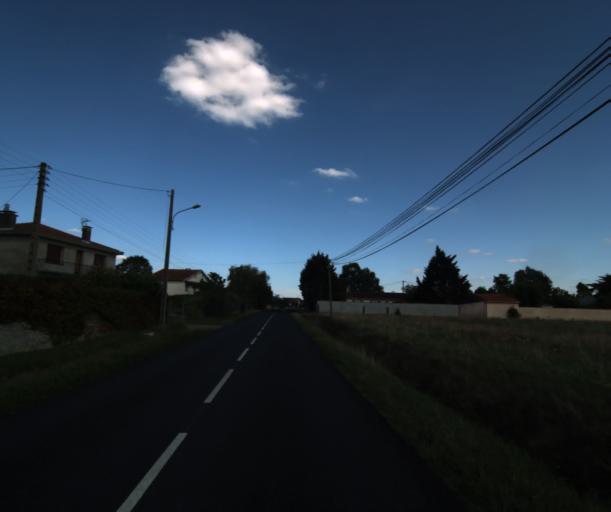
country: FR
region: Midi-Pyrenees
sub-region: Departement de la Haute-Garonne
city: Saint-Lys
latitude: 43.5026
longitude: 1.1915
